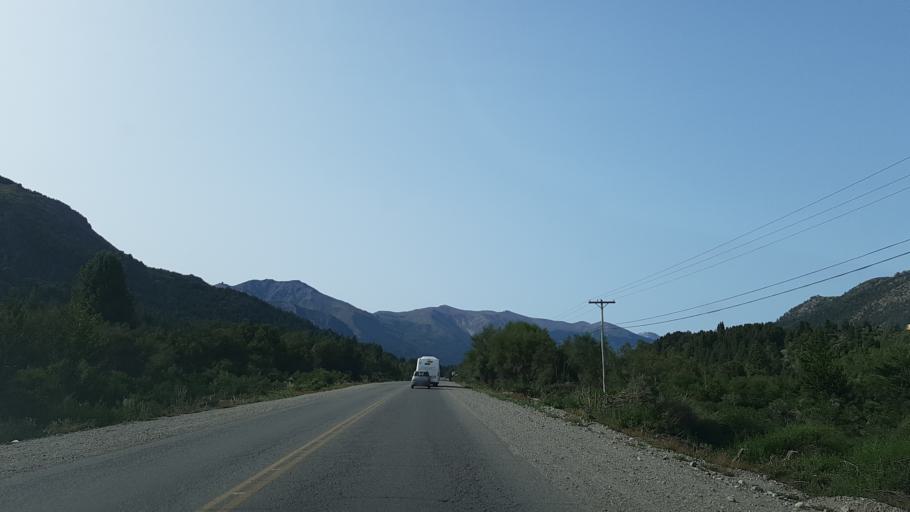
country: AR
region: Rio Negro
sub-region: Departamento de Bariloche
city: San Carlos de Bariloche
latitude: -41.1407
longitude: -71.4112
